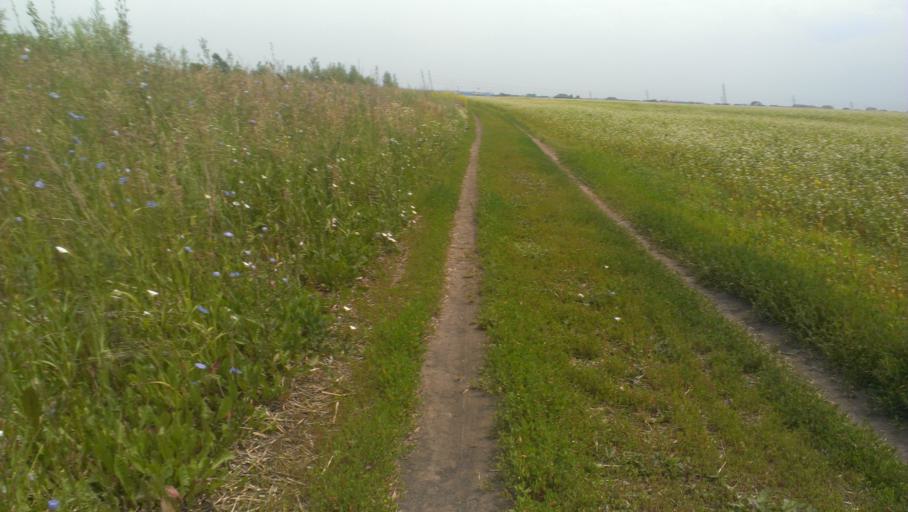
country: RU
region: Altai Krai
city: Novosilikatnyy
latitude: 53.3770
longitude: 83.6405
